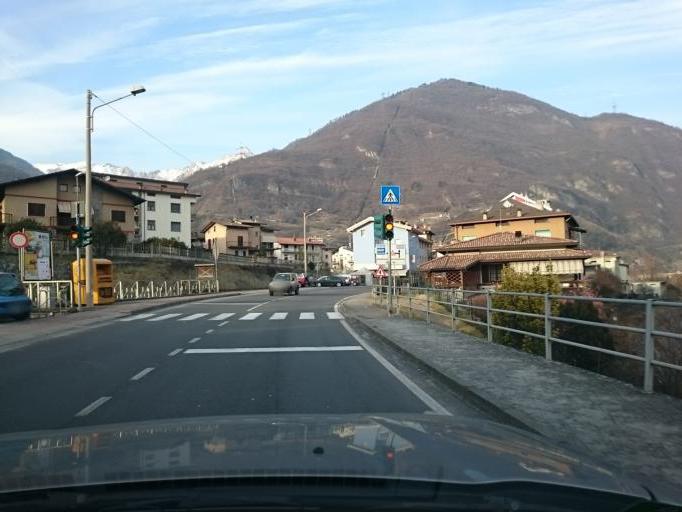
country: IT
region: Lombardy
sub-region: Provincia di Brescia
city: Malegno
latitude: 45.9473
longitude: 10.2769
